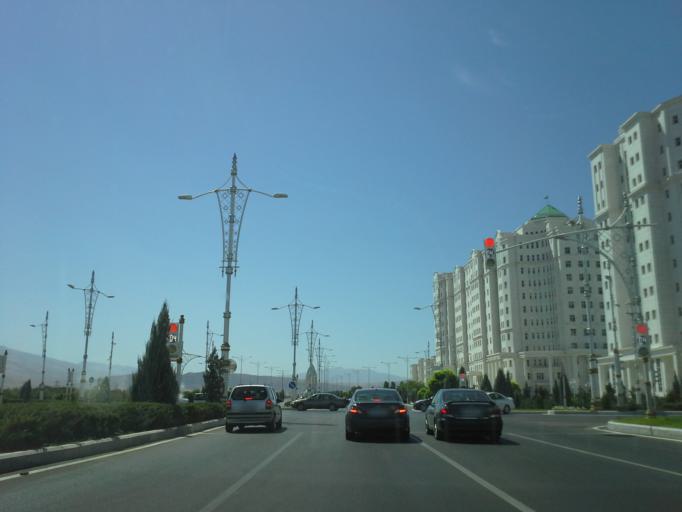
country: TM
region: Ahal
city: Ashgabat
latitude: 37.9136
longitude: 58.3437
